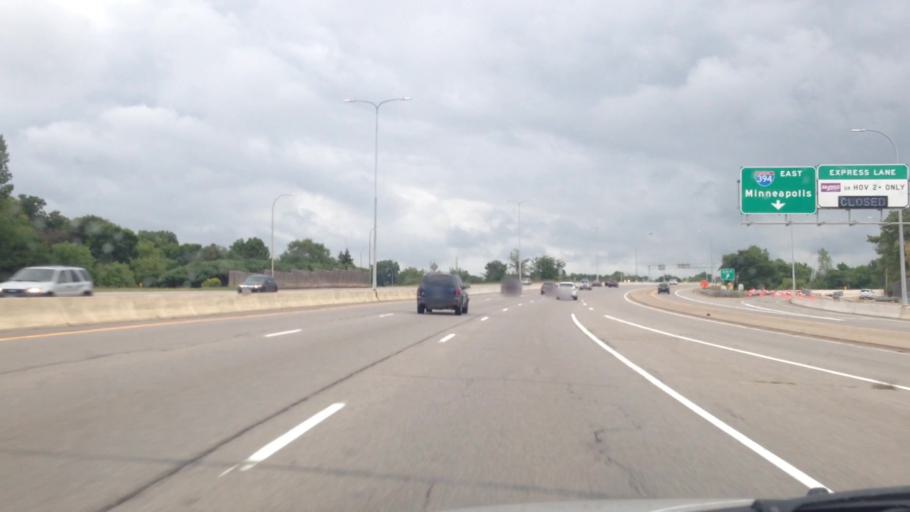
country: US
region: Minnesota
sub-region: Hennepin County
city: Saint Louis Park
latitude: 44.9748
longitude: -93.3419
